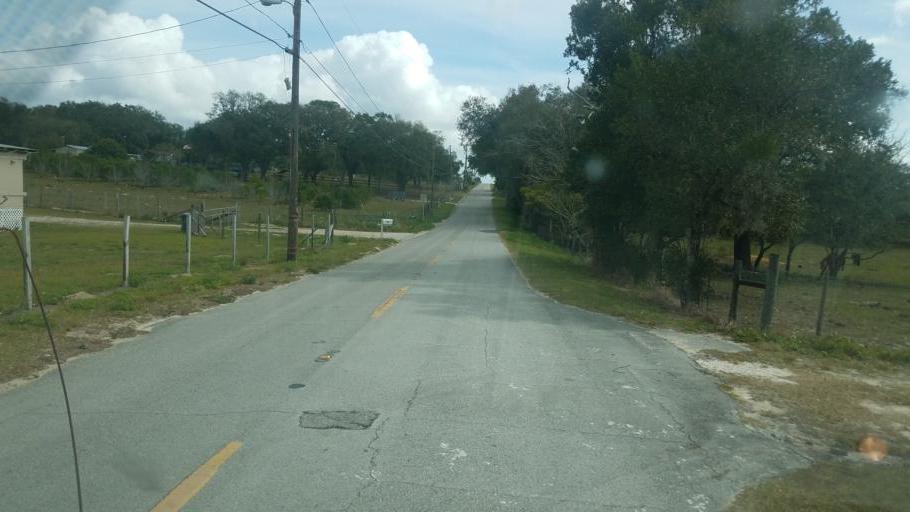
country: US
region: Florida
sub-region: Polk County
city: Dundee
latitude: 28.0333
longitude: -81.6076
